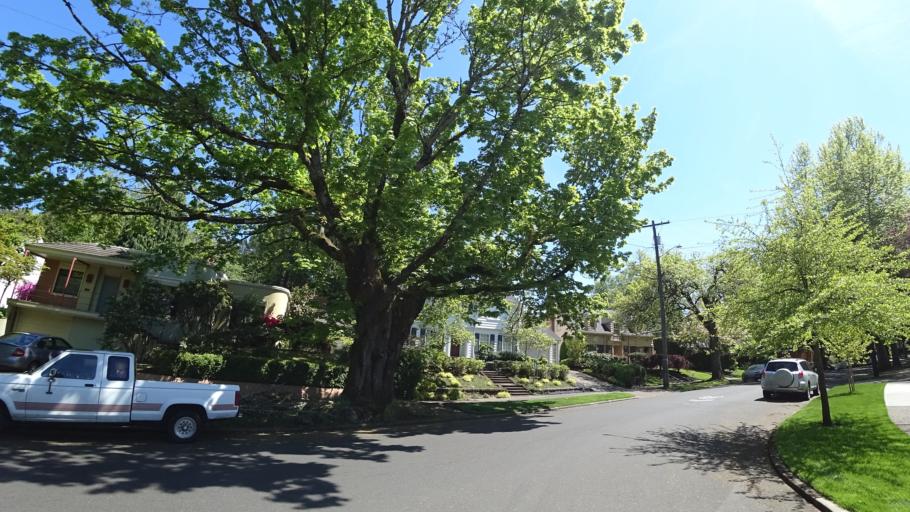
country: US
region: Oregon
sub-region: Clackamas County
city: Milwaukie
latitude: 45.4776
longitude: -122.6307
